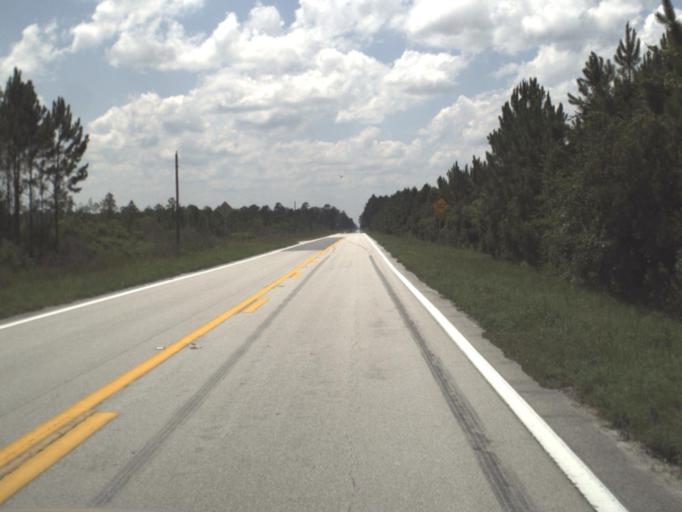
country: US
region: Florida
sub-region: Baker County
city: Macclenny
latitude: 30.5137
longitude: -82.2702
